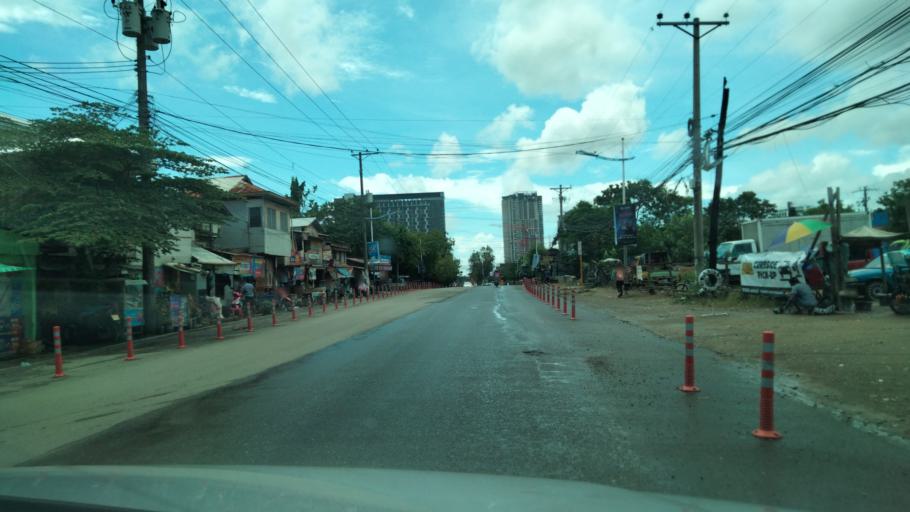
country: PH
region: Central Visayas
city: Mandaue City
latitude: 10.3281
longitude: 123.9336
